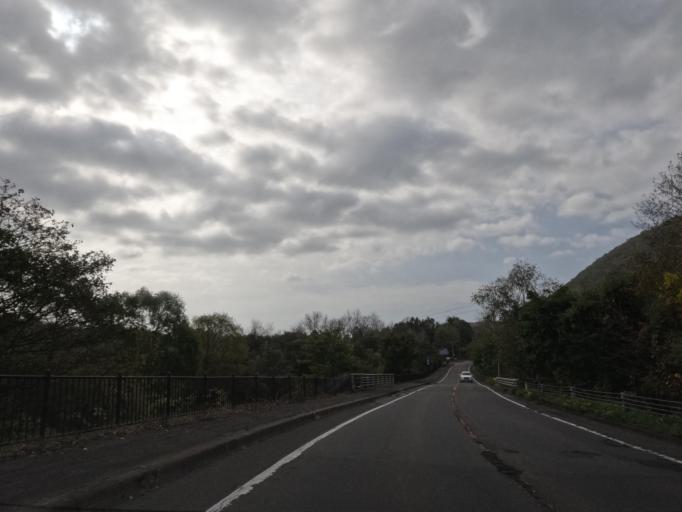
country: JP
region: Hokkaido
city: Date
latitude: 42.5444
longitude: 140.8576
